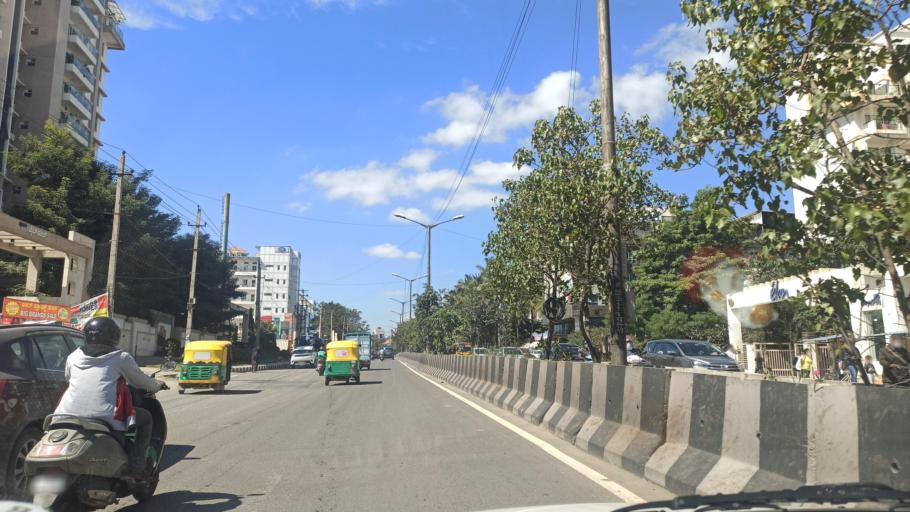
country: IN
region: Karnataka
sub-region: Bangalore Urban
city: Bangalore
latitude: 12.9171
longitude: 77.6730
